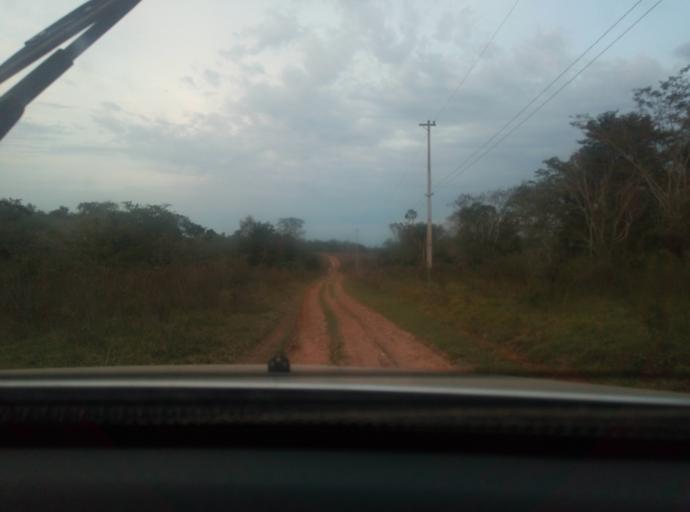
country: PY
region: Caaguazu
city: Carayao
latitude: -25.1485
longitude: -56.3873
